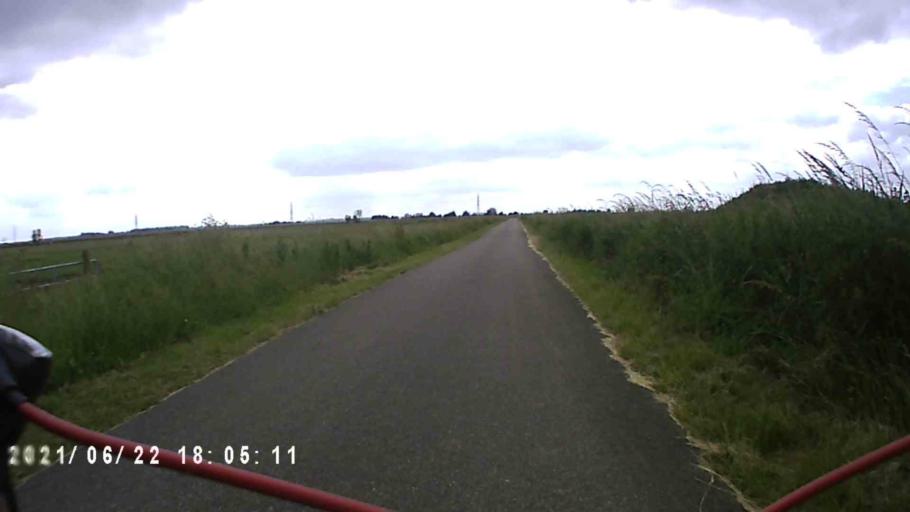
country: NL
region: Groningen
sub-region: Gemeente Groningen
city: Groningen
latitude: 53.1916
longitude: 6.5074
